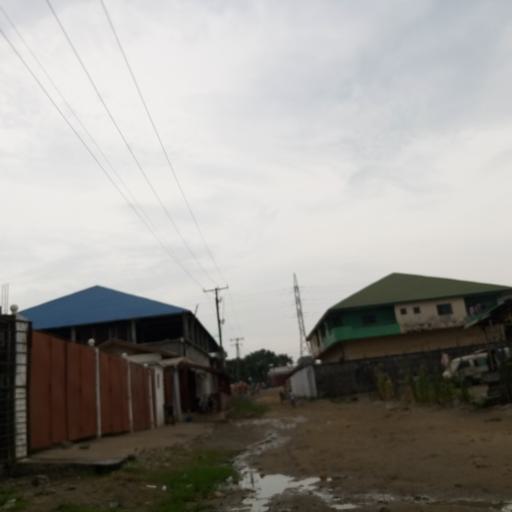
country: LR
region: Montserrado
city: Monrovia
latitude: 6.2949
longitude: -10.6848
